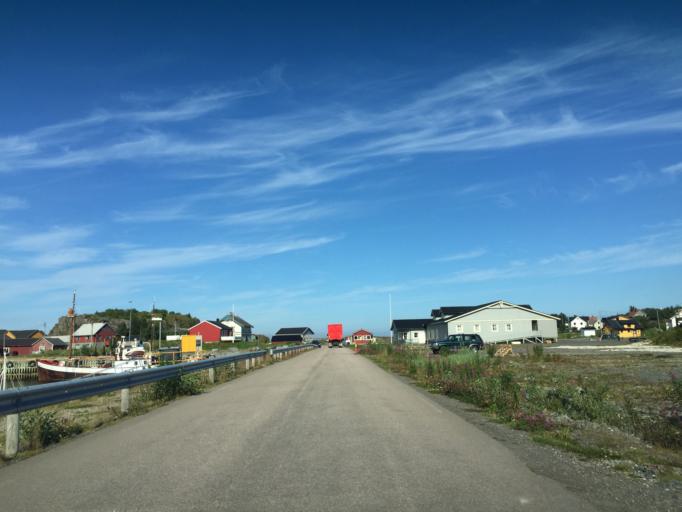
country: NO
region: Nordland
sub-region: Vagan
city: Kabelvag
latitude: 68.3861
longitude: 14.4176
